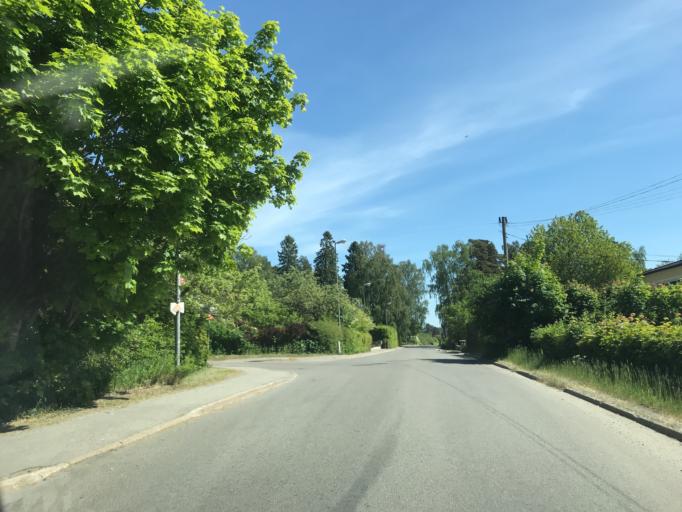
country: SE
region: Stockholm
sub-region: Sollentuna Kommun
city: Sollentuna
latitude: 59.4190
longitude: 17.9740
